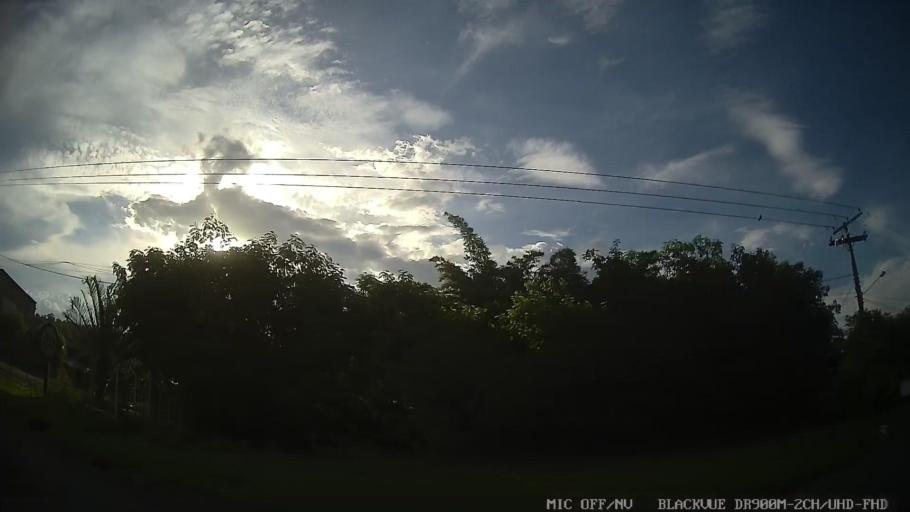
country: BR
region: Sao Paulo
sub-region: Tiete
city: Tiete
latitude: -23.0916
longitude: -47.7221
